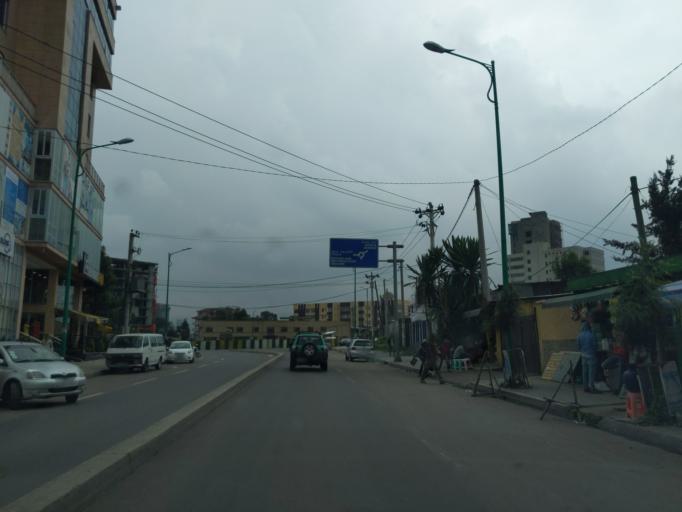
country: ET
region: Adis Abeba
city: Addis Ababa
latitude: 8.9867
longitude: 38.7652
